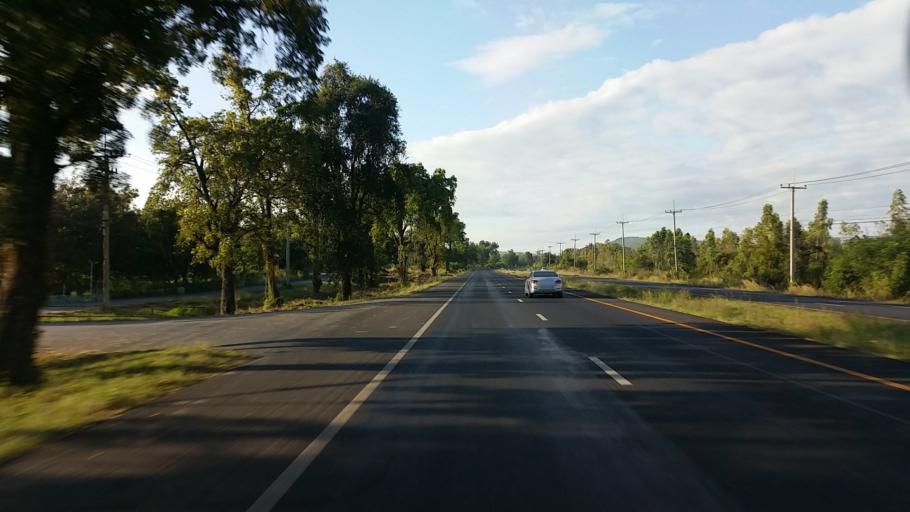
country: TH
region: Lop Buri
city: Phatthana Nikhom
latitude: 14.9948
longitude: 100.9355
